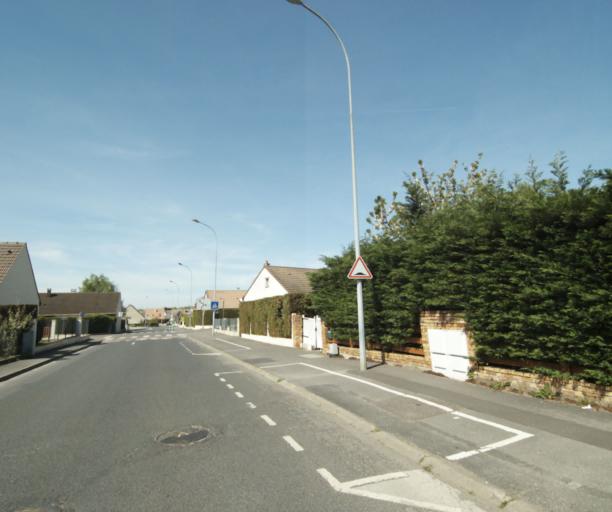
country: FR
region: Ile-de-France
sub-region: Departement de Seine-et-Marne
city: Nangis
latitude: 48.5502
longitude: 3.0110
